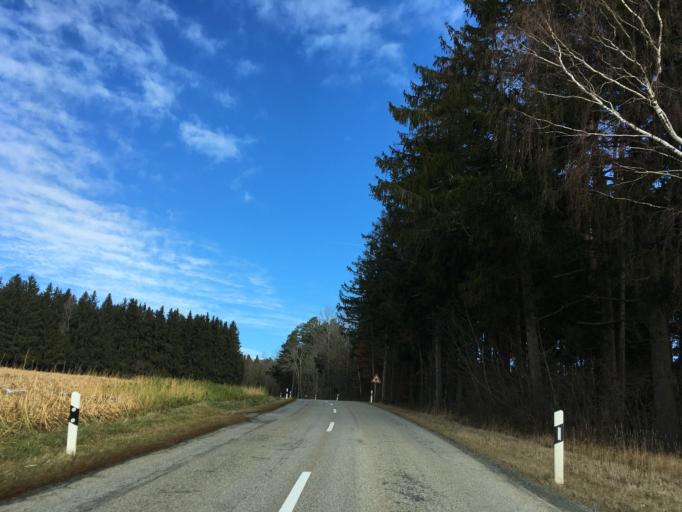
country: DE
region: Bavaria
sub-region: Upper Bavaria
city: Reichertsheim
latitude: 48.2100
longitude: 12.2620
